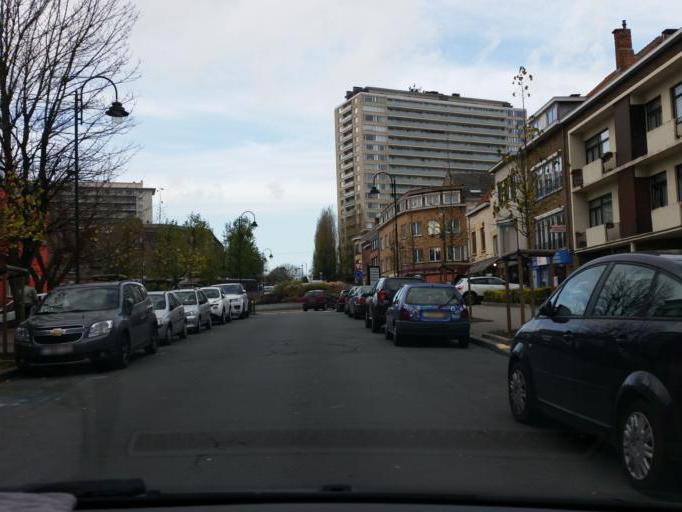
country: BE
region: Flanders
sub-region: Provincie Vlaams-Brabant
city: Grimbergen
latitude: 50.8991
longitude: 4.3609
